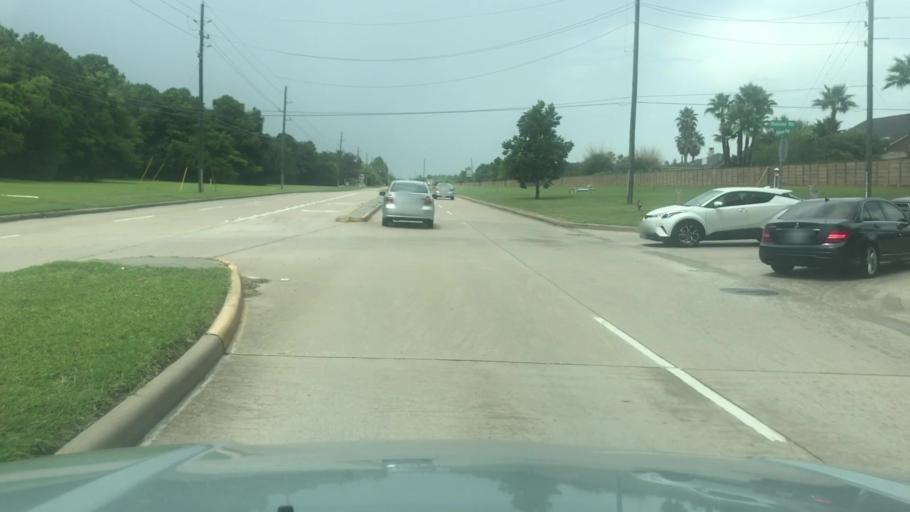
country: US
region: Texas
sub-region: Harris County
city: Katy
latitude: 29.7530
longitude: -95.8018
